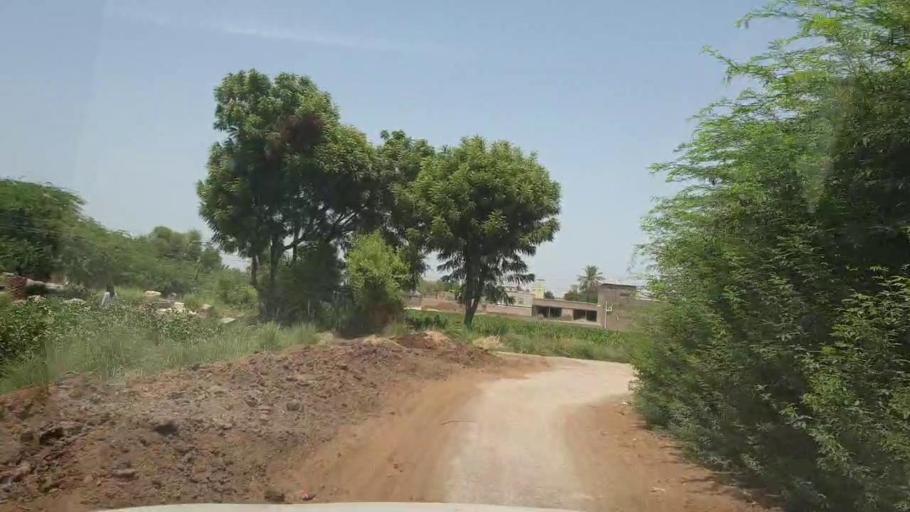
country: PK
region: Sindh
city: Bozdar
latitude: 27.1810
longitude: 68.6330
